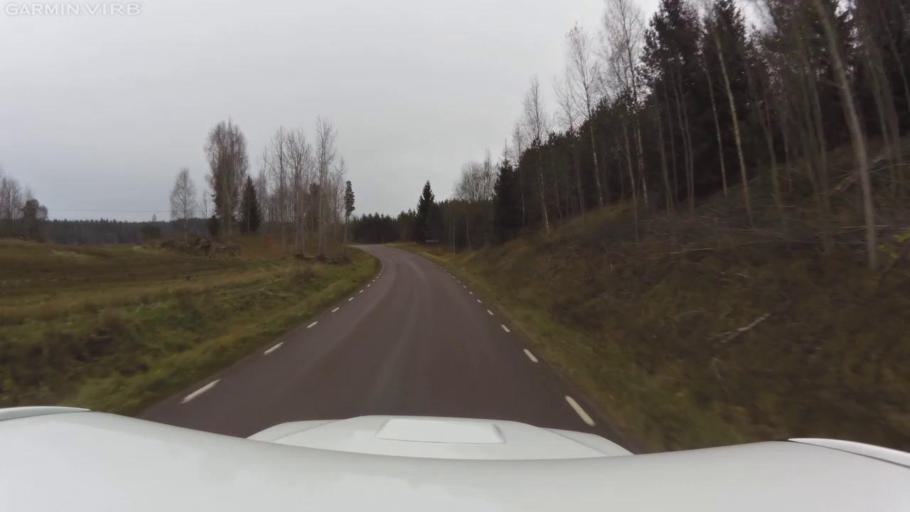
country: SE
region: OEstergoetland
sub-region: Mjolby Kommun
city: Mantorp
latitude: 58.1542
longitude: 15.3899
